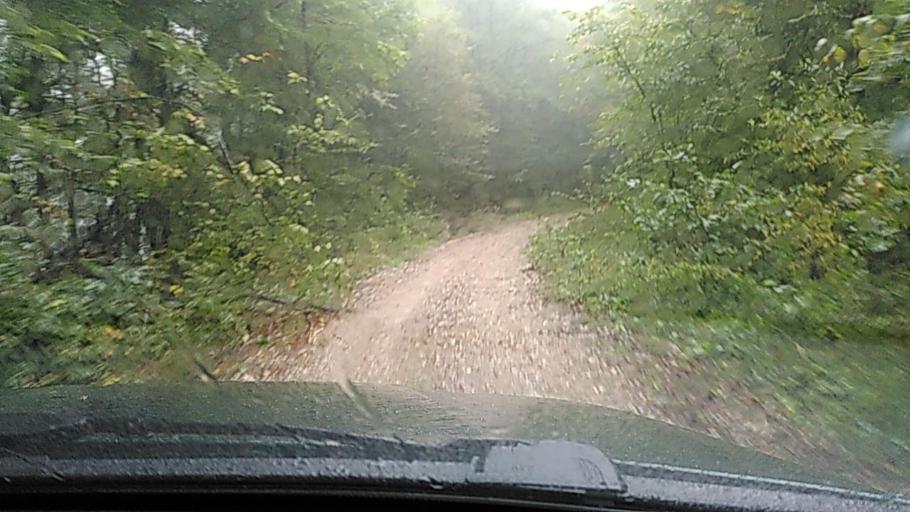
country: RU
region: Kabardino-Balkariya
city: Belaya Rechka
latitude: 43.3746
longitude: 43.4289
